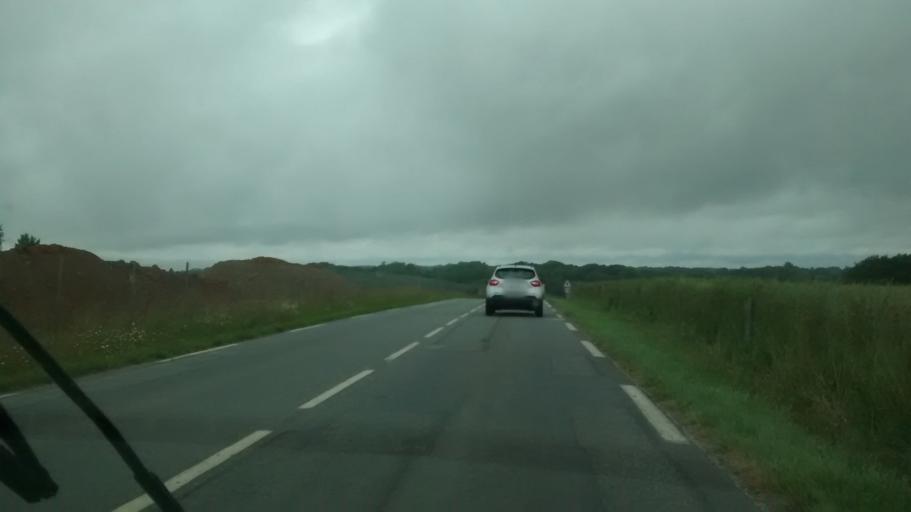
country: FR
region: Brittany
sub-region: Departement du Morbihan
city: Queven
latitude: 47.7610
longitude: -3.4238
